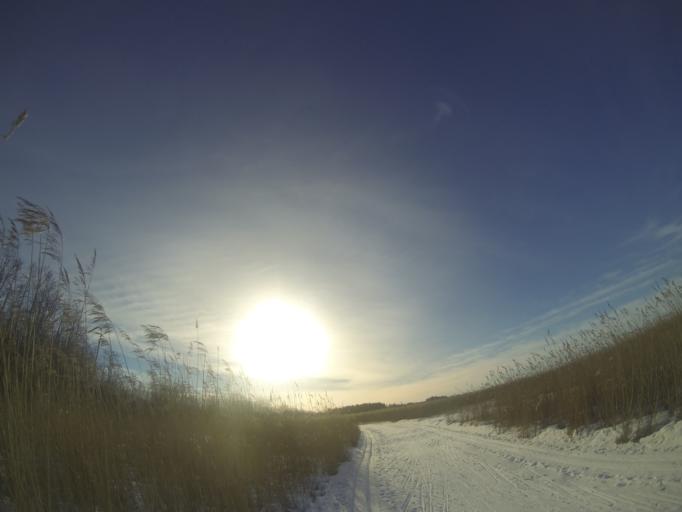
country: FI
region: Southern Savonia
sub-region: Savonlinna
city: Savonlinna
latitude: 61.9107
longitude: 28.9198
